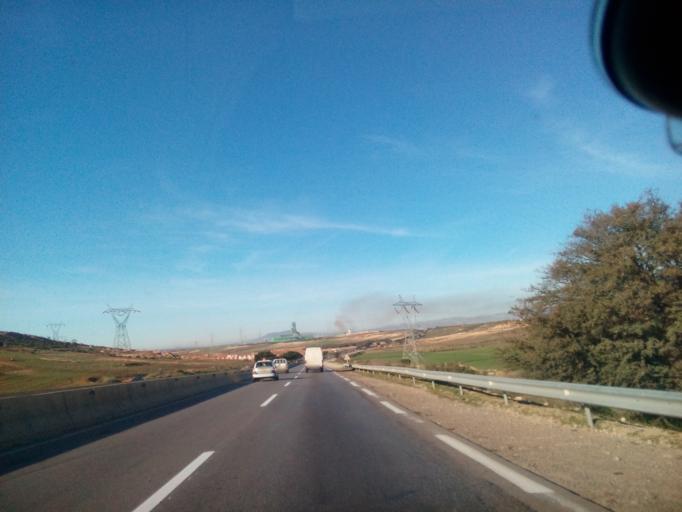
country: DZ
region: Oran
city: Ain el Bya
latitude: 35.7676
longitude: -0.2259
